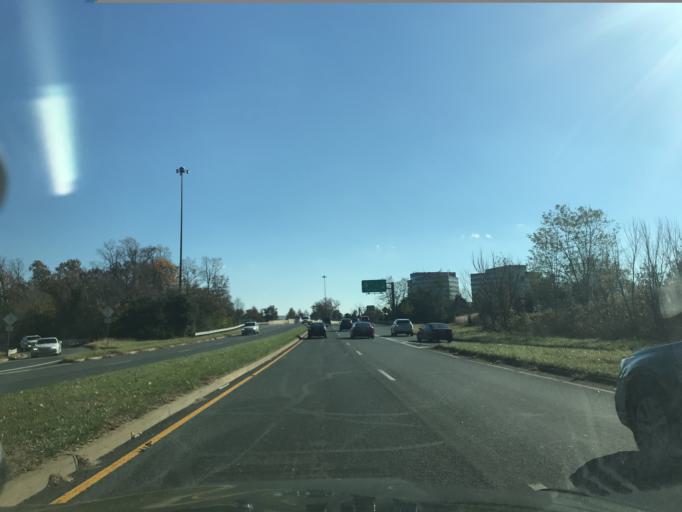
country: US
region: Virginia
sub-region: Fairfax County
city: Greenbriar
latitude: 38.8704
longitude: -77.3656
